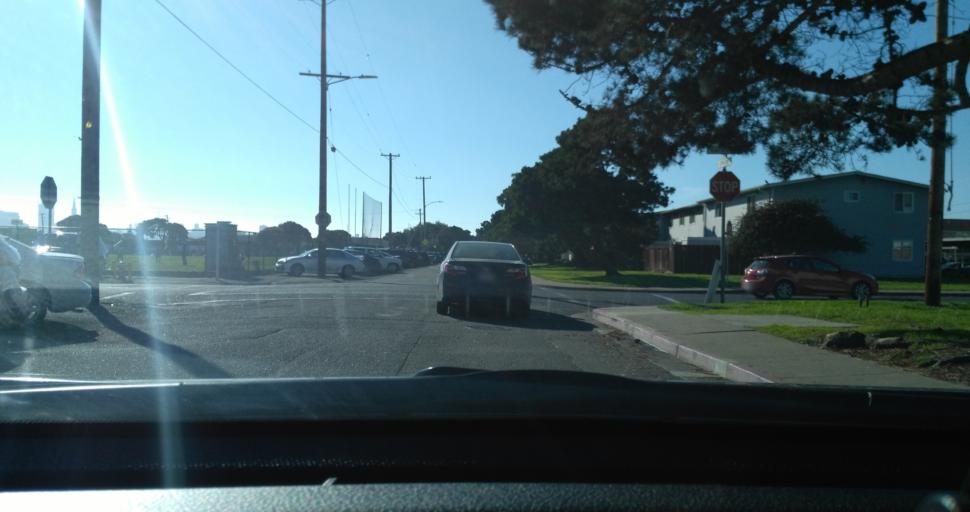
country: US
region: California
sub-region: San Francisco County
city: San Francisco
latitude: 37.8285
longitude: -122.3718
